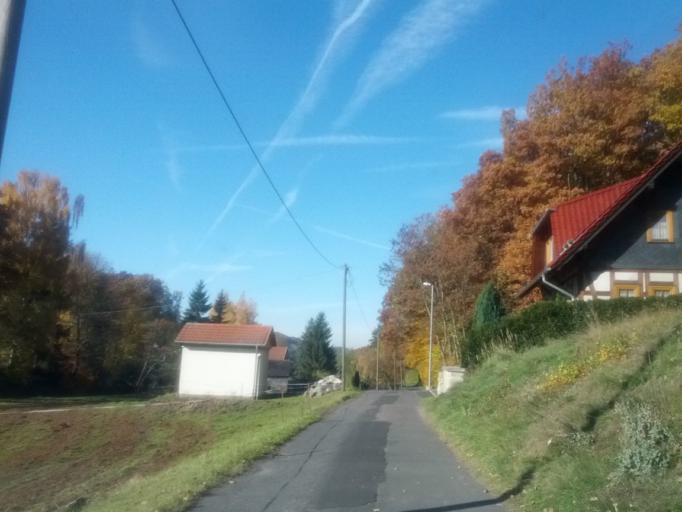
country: DE
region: Thuringia
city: Seebach
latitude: 50.9254
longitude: 10.4448
